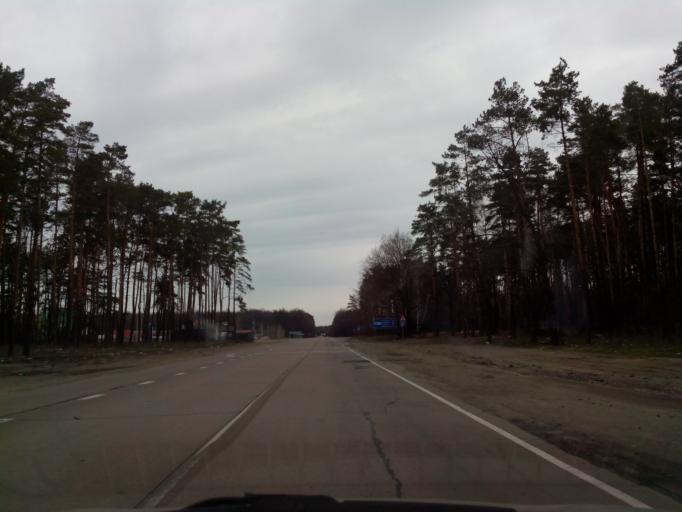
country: RU
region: Tambov
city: Bokino
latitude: 52.5570
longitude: 41.3551
